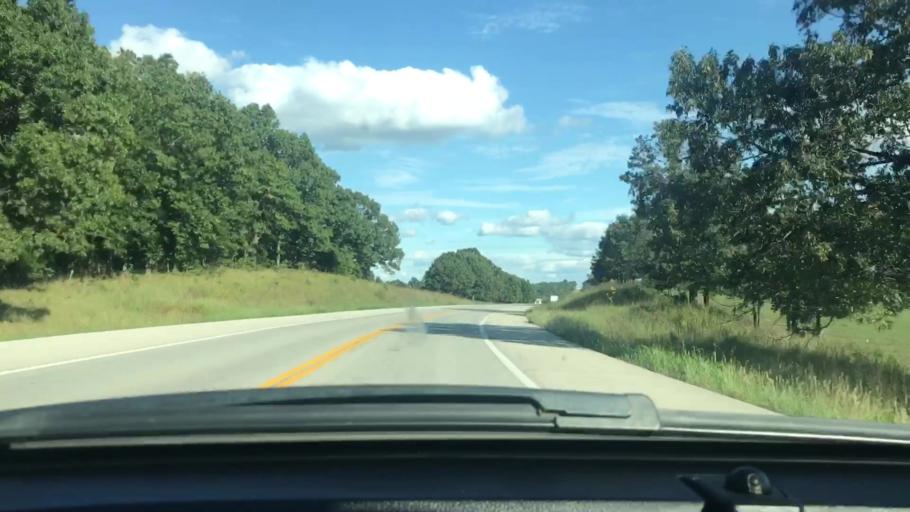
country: US
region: Missouri
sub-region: Howell County
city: West Plains
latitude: 36.6607
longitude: -91.7091
